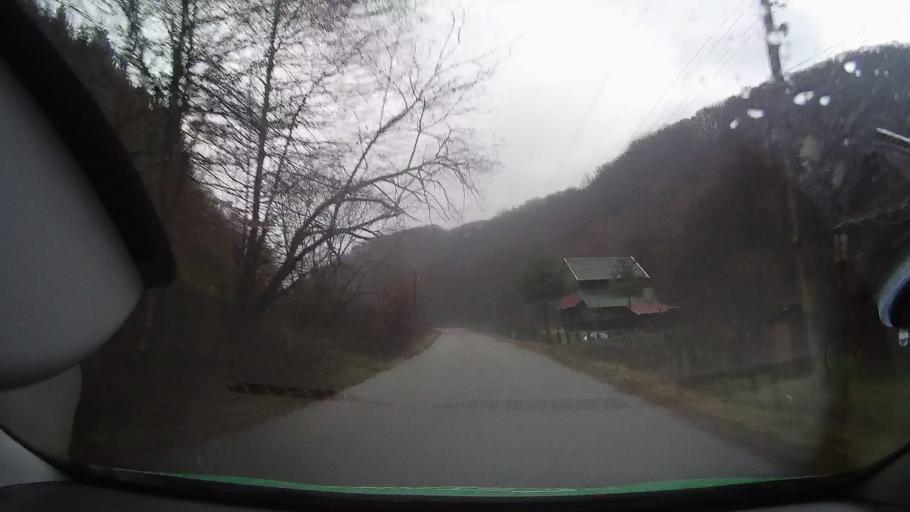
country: RO
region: Alba
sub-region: Comuna Avram Iancu
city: Avram Iancu
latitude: 46.2906
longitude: 22.7514
